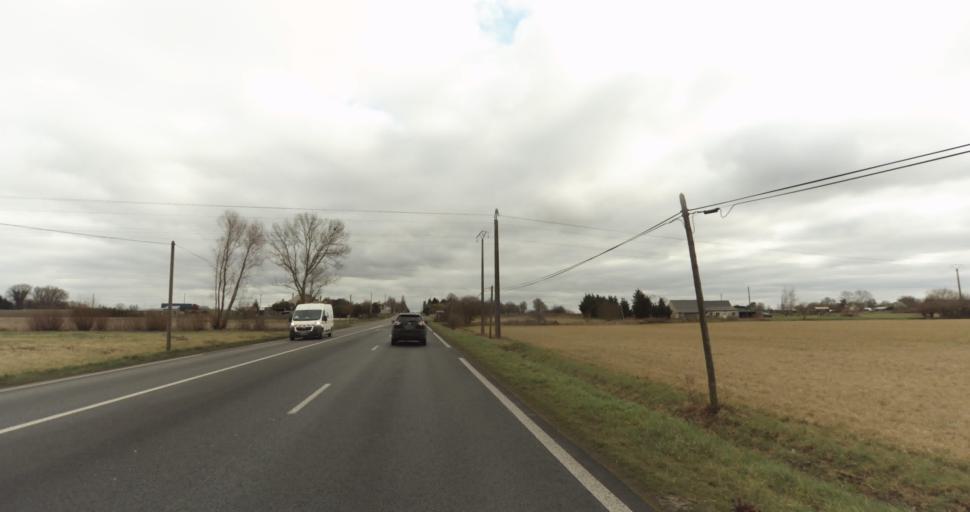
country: FR
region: Pays de la Loire
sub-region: Departement de Maine-et-Loire
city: Vivy
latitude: 47.3635
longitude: -0.0920
